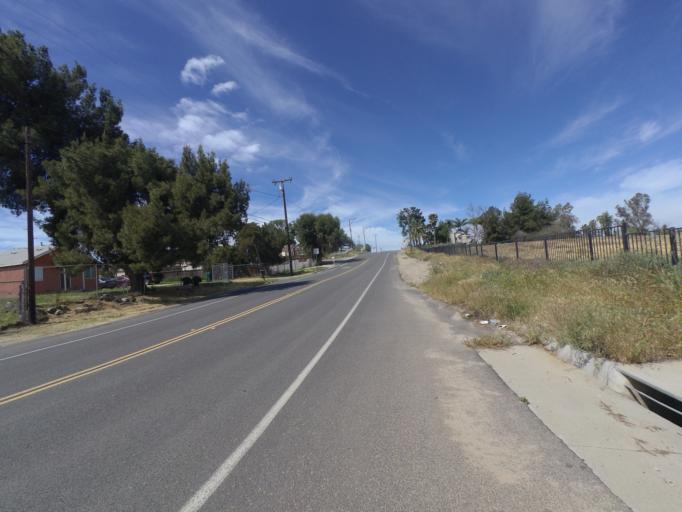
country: US
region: California
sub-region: Riverside County
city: March Air Force Base
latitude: 33.9206
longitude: -117.2770
